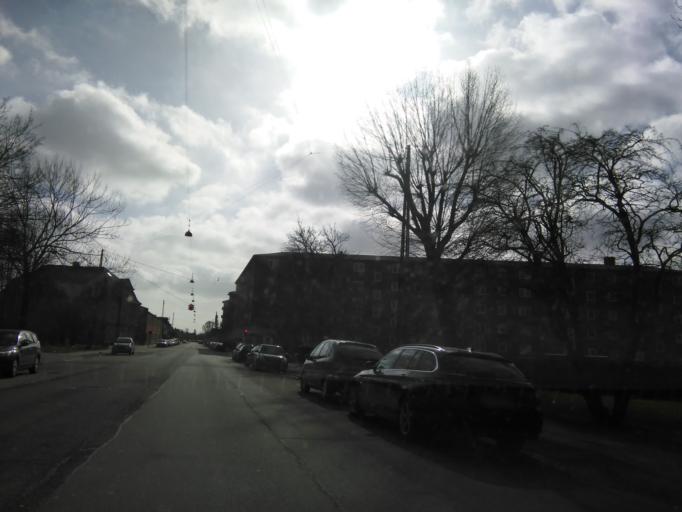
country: DK
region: Capital Region
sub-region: Kobenhavn
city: Christianshavn
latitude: 55.6622
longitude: 12.6242
